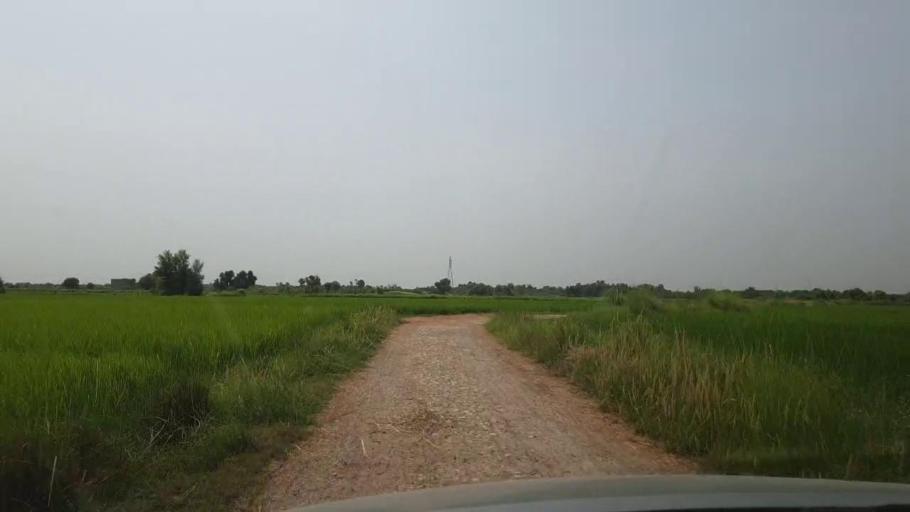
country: PK
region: Sindh
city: Madeji
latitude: 27.7905
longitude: 68.5384
